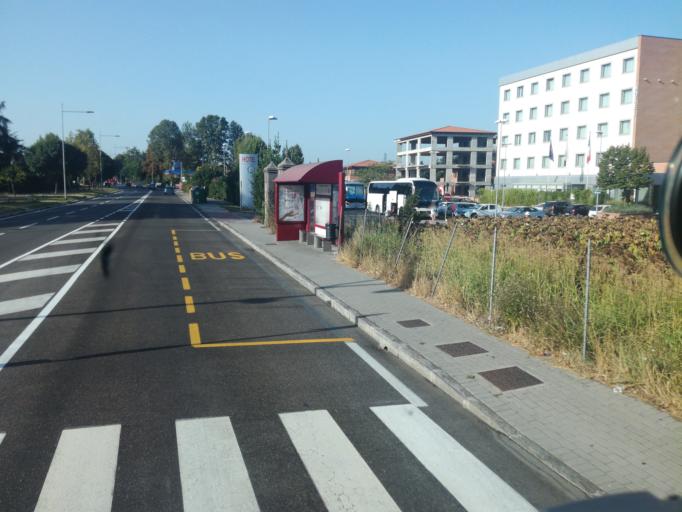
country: IT
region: Emilia-Romagna
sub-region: Provincia di Bologna
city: Progresso
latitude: 44.5335
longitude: 11.3676
